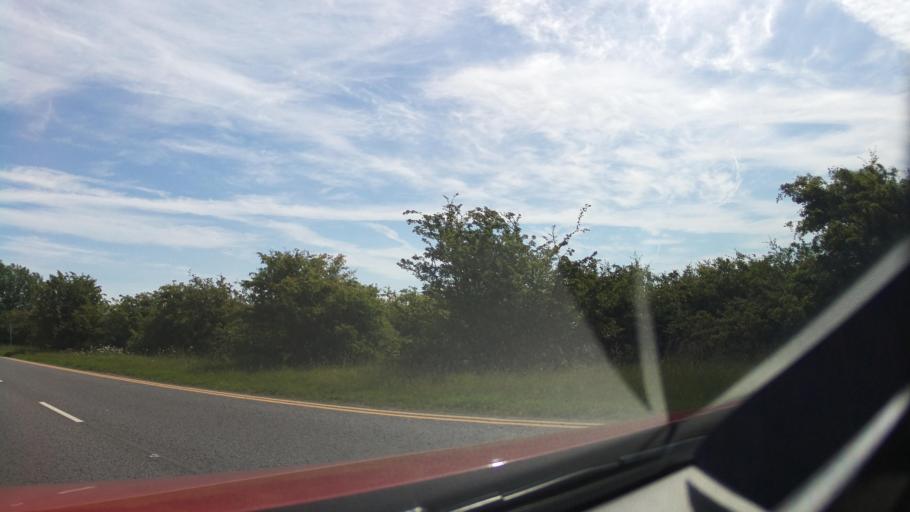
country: GB
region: England
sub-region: Lincolnshire
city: Burton
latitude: 53.3129
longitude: -0.5328
